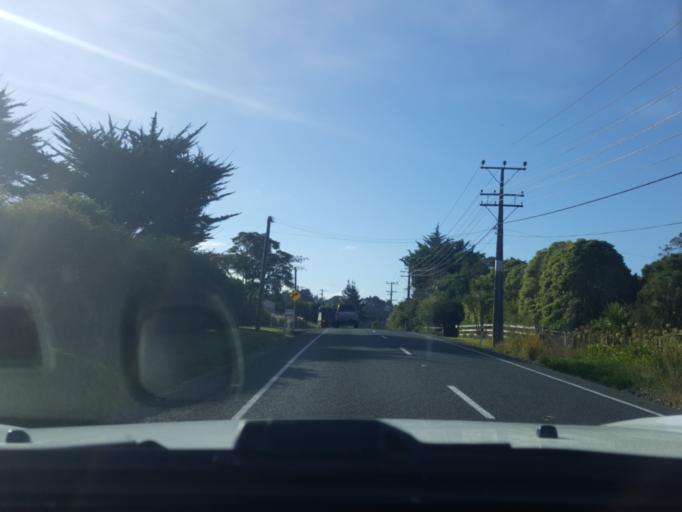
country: NZ
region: Auckland
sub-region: Auckland
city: Muriwai Beach
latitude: -36.7646
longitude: 174.5768
